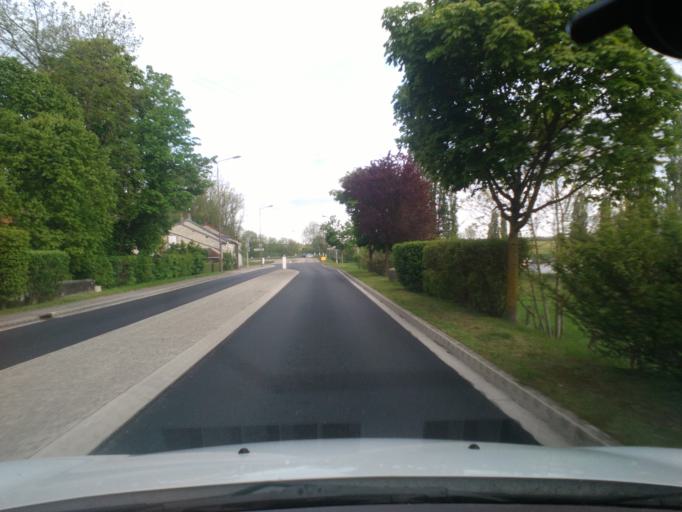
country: FR
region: Champagne-Ardenne
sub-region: Departement de la Haute-Marne
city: Lavilleneuve-au-Roi
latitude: 48.1847
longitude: 4.9762
